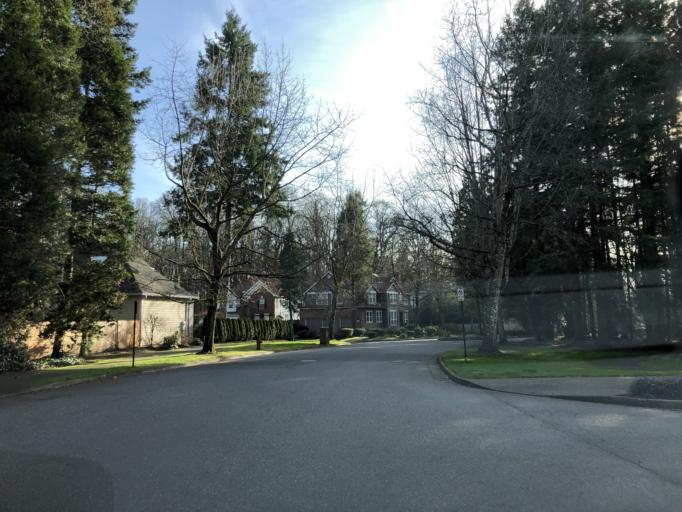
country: US
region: Oregon
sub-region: Washington County
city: Durham
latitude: 45.4221
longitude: -122.7375
